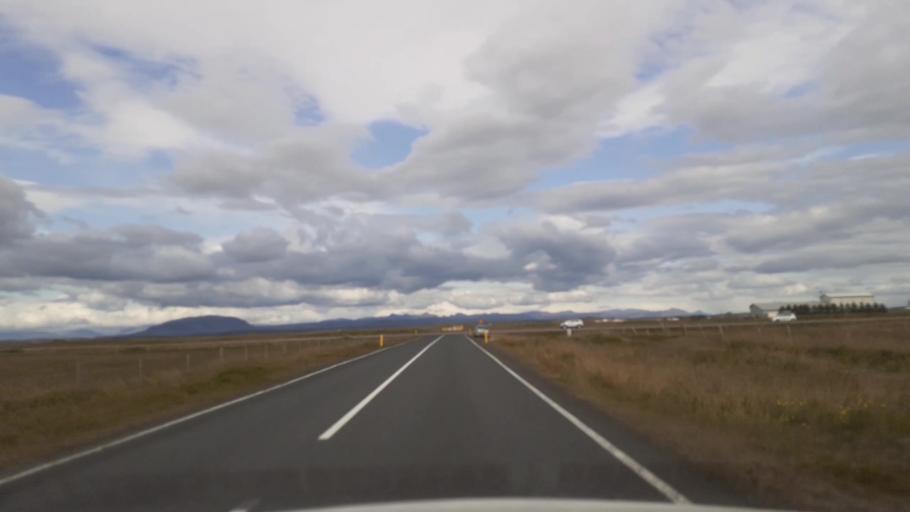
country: IS
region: South
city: Selfoss
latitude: 63.9425
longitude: -20.8383
